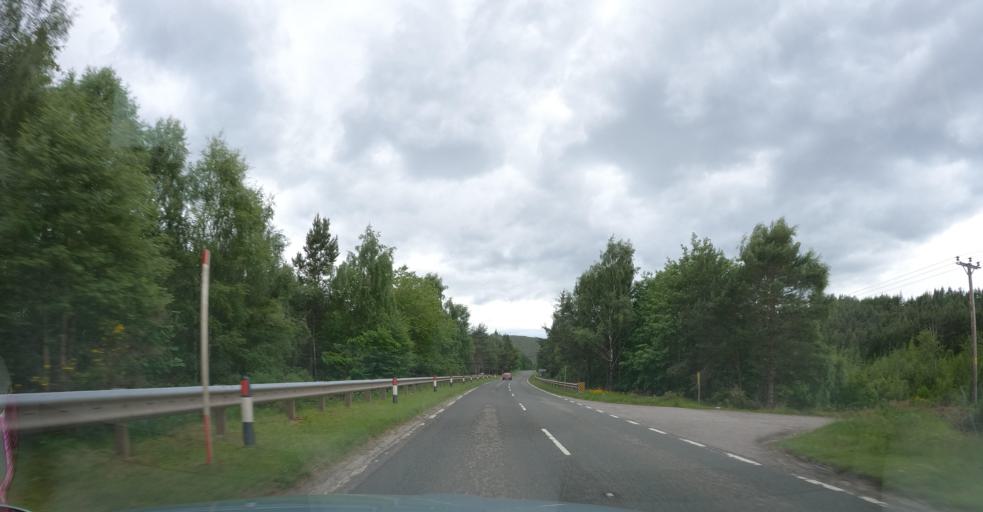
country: GB
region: Scotland
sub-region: Highland
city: Muir of Ord
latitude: 57.6339
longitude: -4.6813
